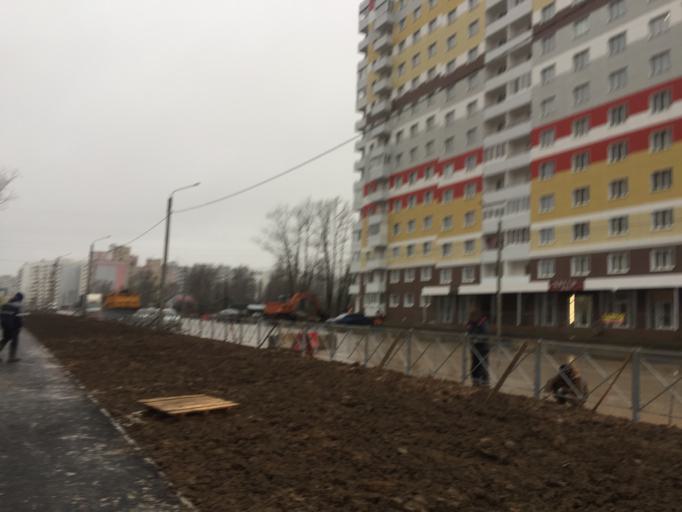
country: RU
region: Jaroslavl
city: Yaroslavl
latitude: 57.6986
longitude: 39.7877
